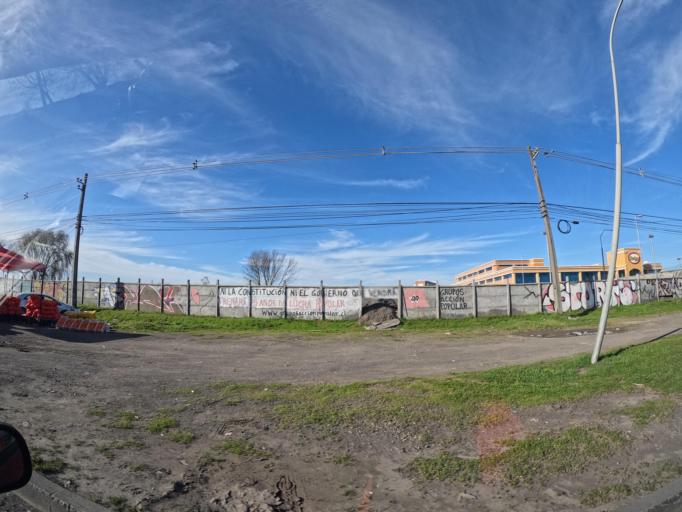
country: CL
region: Biobio
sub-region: Provincia de Concepcion
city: Concepcion
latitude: -36.7775
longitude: -73.0787
